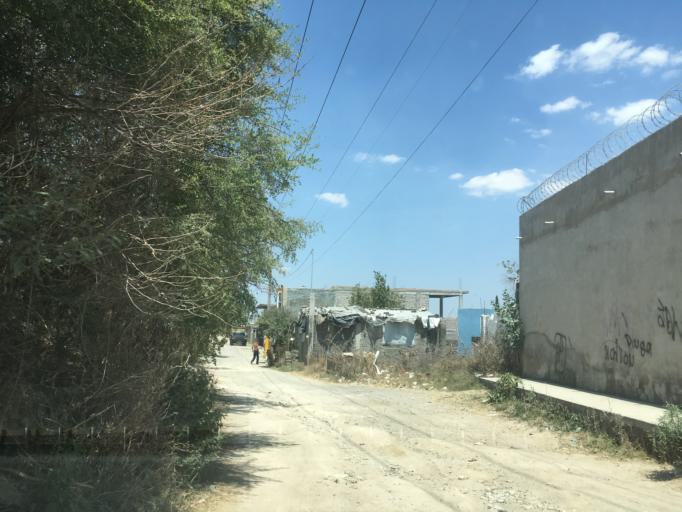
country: MX
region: Michoacan
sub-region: Morelia
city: San Antonio
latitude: 19.6703
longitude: -101.2552
